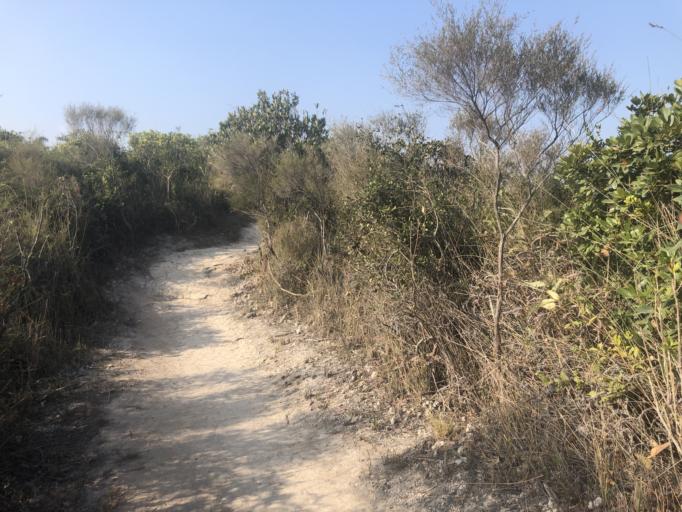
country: HK
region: Sai Kung
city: Sai Kung
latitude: 22.3608
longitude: 114.2946
